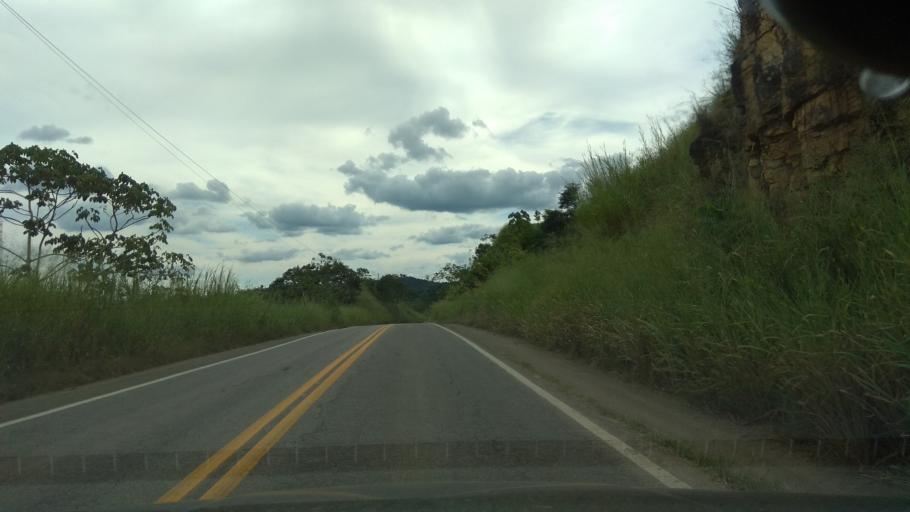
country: BR
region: Bahia
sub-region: Ipiau
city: Ipiau
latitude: -14.1551
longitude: -39.6968
